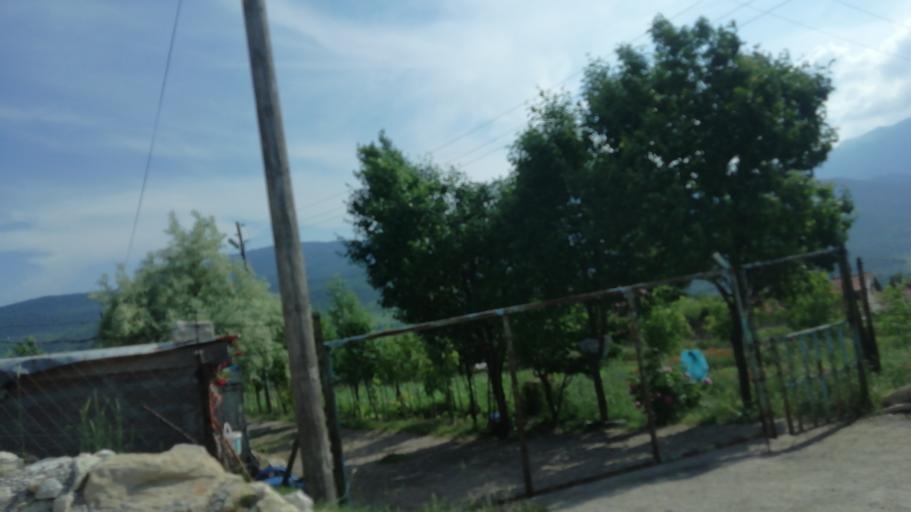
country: TR
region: Karabuk
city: Karabuk
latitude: 41.1167
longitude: 32.5765
